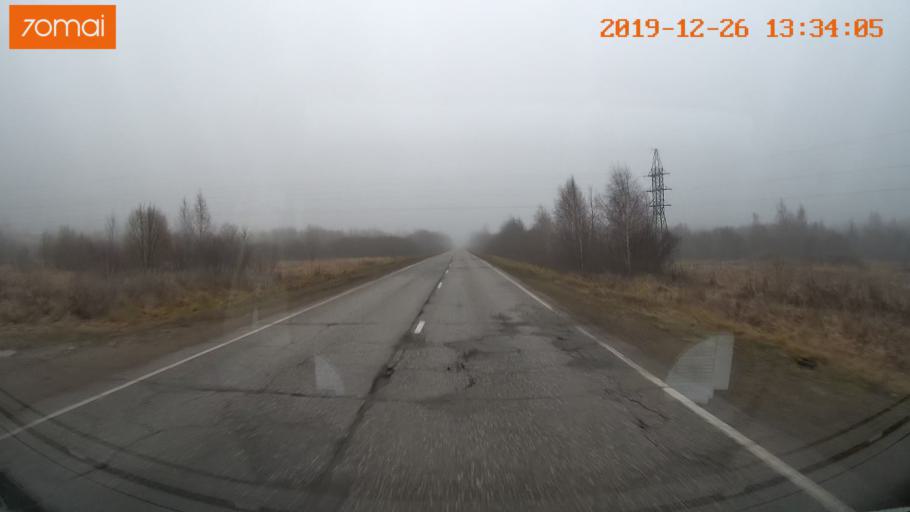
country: RU
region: Vologda
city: Sheksna
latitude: 58.8101
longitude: 38.3175
